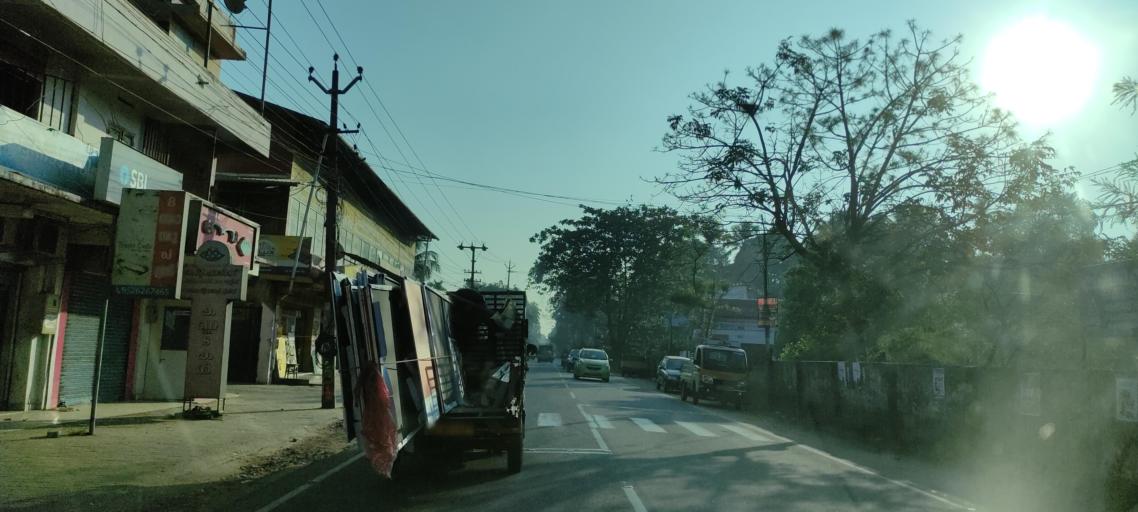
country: IN
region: Kerala
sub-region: Alappuzha
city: Kattanam
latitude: 9.1774
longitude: 76.5300
